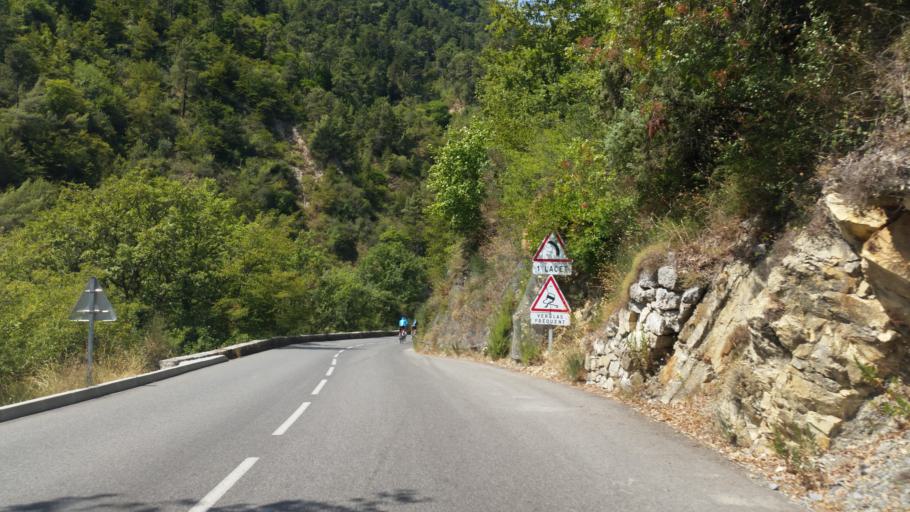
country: FR
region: Provence-Alpes-Cote d'Azur
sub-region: Departement des Alpes-Maritimes
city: Sainte-Agnes
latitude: 43.8295
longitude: 7.4759
